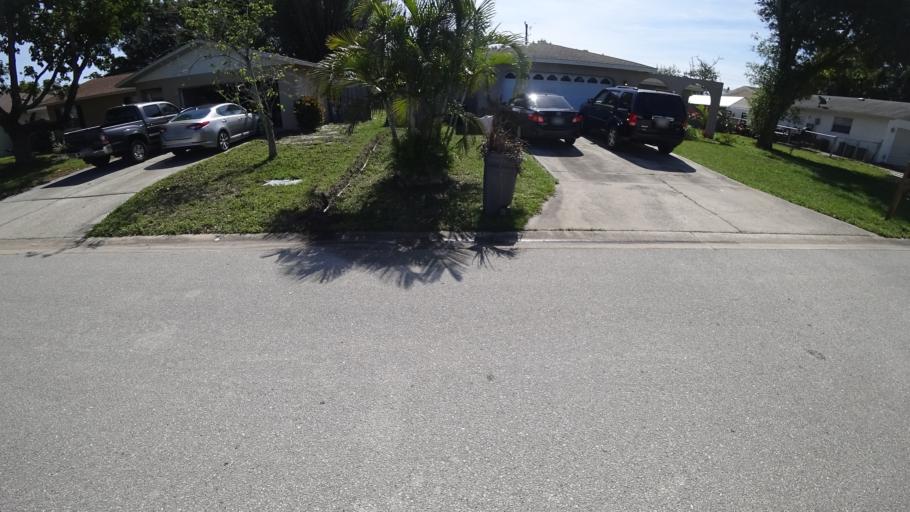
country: US
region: Florida
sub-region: Manatee County
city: West Bradenton
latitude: 27.5088
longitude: -82.6288
